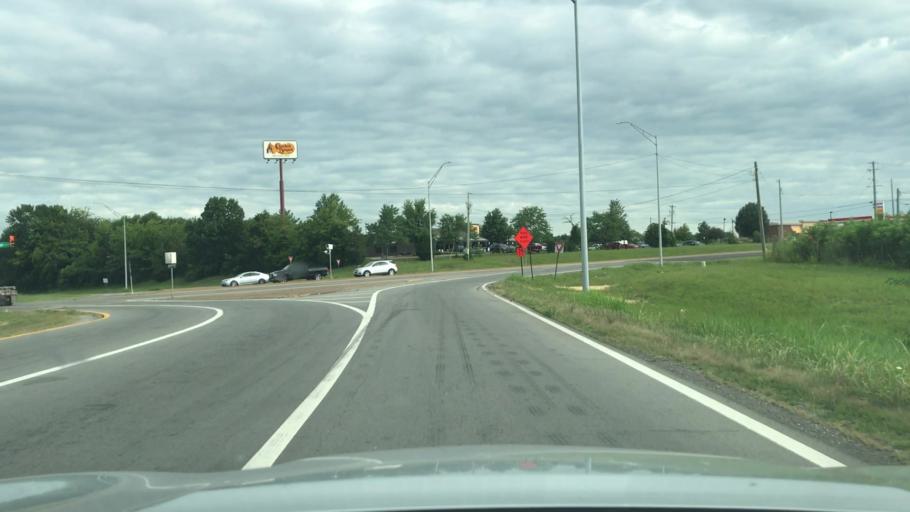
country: US
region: Tennessee
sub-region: Montgomery County
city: Clarksville
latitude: 36.6008
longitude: -87.2806
